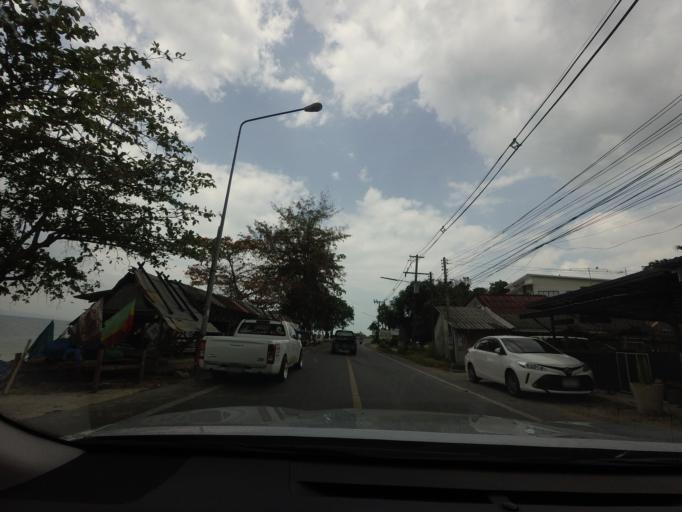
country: TH
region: Phangnga
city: Ban Ao Nang
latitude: 8.0647
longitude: 98.7444
